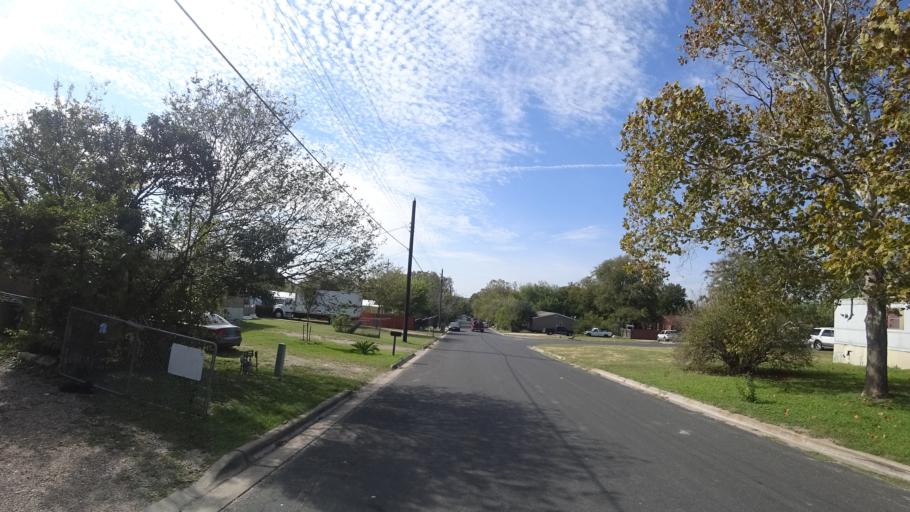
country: US
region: Texas
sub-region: Travis County
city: Pflugerville
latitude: 30.4086
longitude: -97.6318
